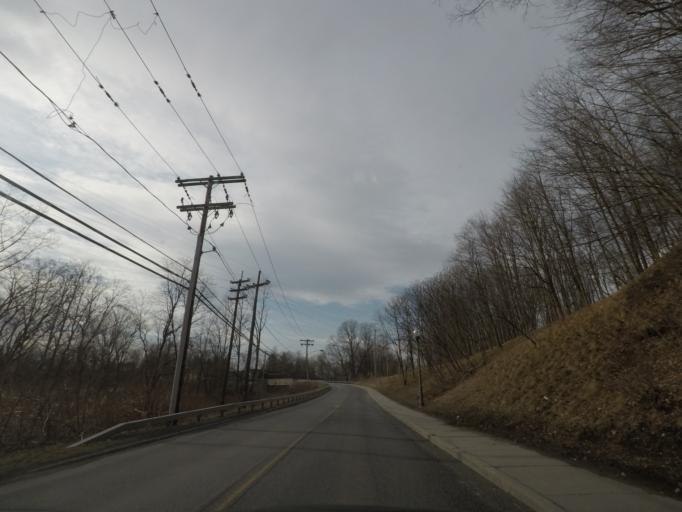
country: US
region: New York
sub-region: Rensselaer County
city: Hoosick Falls
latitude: 42.9047
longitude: -73.3538
